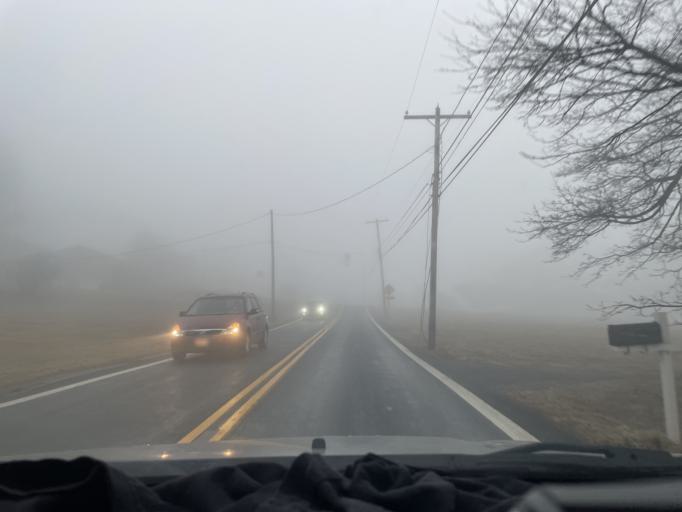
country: US
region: Maryland
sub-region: Washington County
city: Highfield-Cascade
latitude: 39.6984
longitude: -77.4853
